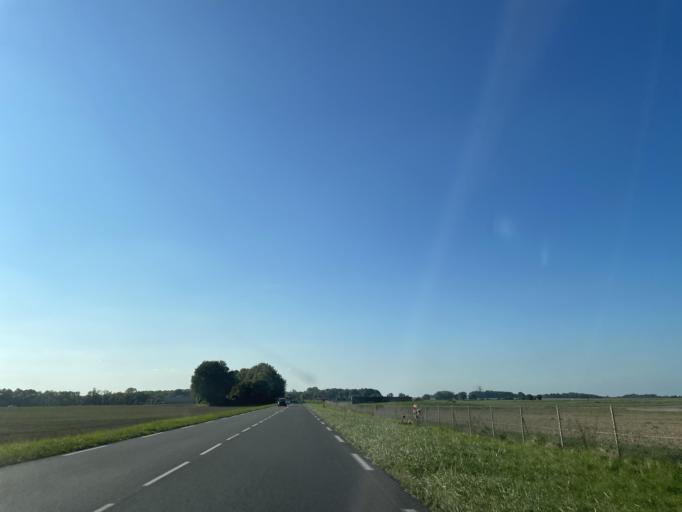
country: FR
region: Ile-de-France
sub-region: Departement de Seine-et-Marne
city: Pommeuse
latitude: 48.8347
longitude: 2.9946
